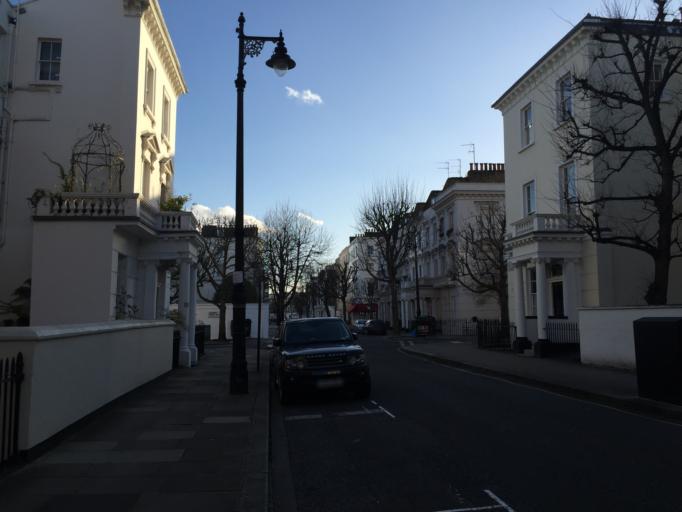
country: GB
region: England
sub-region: Greater London
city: Battersea
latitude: 51.4896
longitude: -0.1429
